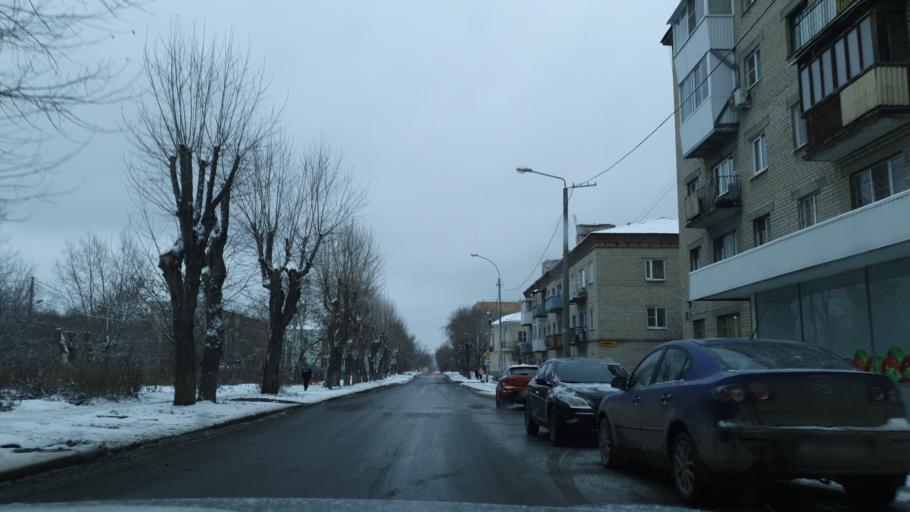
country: RU
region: Sverdlovsk
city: Istok
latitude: 56.7504
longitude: 60.7093
